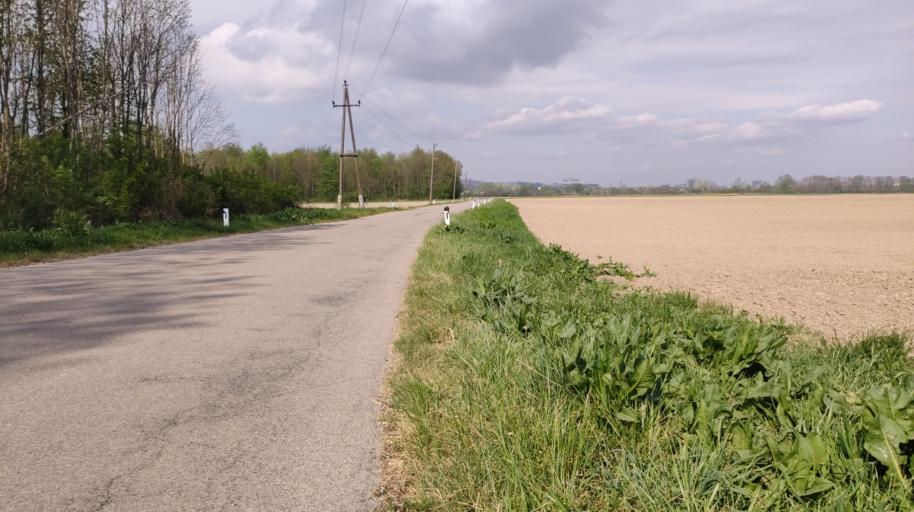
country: AT
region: Burgenland
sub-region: Politischer Bezirk Neusiedl am See
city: Kittsee
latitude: 48.1149
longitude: 17.0558
